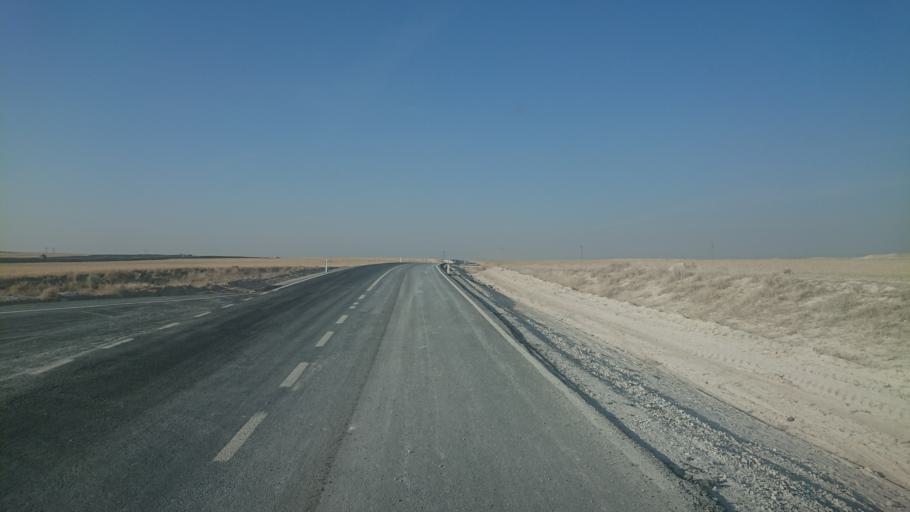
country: TR
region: Aksaray
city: Sultanhani
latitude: 38.0857
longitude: 33.6145
